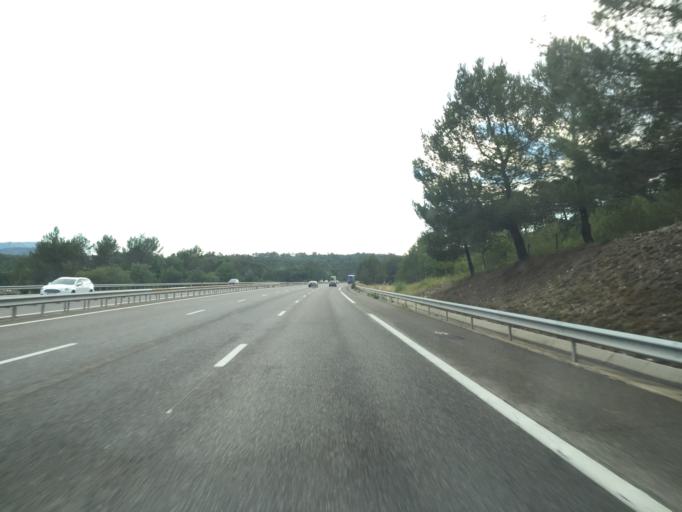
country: FR
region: Provence-Alpes-Cote d'Azur
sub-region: Departement du Var
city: Tourves
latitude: 43.4241
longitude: 5.9674
